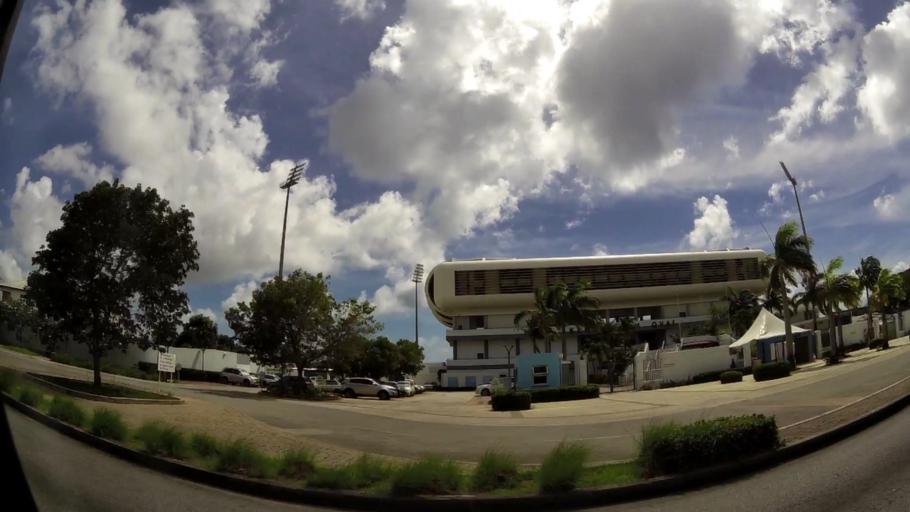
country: BB
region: Saint Michael
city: Bridgetown
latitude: 13.1066
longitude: -59.6228
